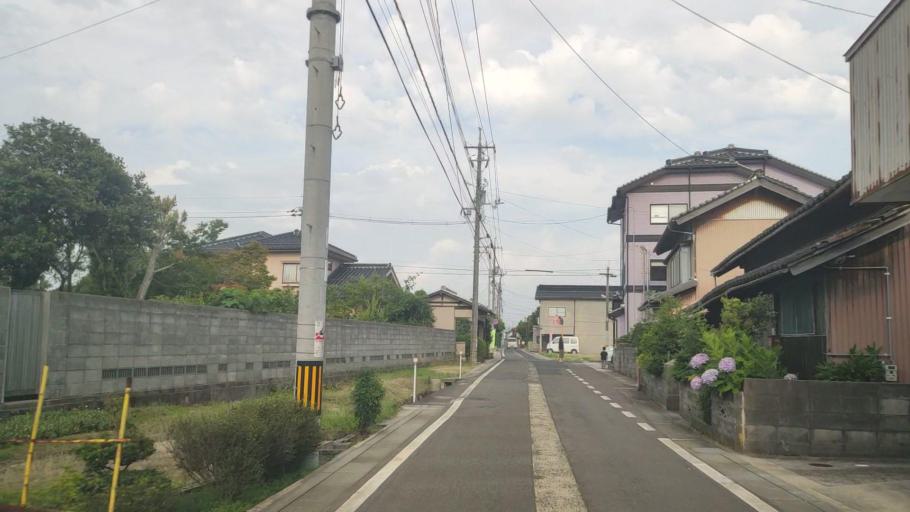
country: JP
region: Tottori
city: Kurayoshi
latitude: 35.4840
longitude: 133.8096
